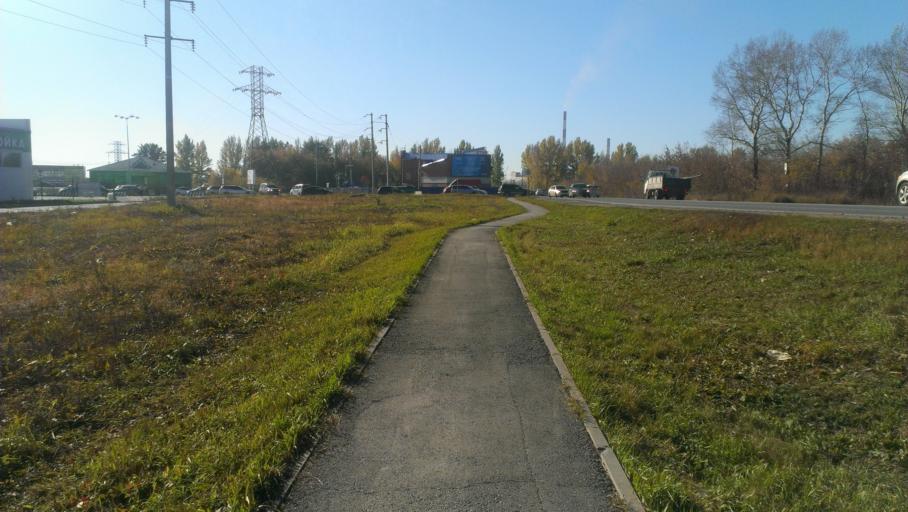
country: RU
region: Altai Krai
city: Novosilikatnyy
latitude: 53.3507
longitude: 83.6308
